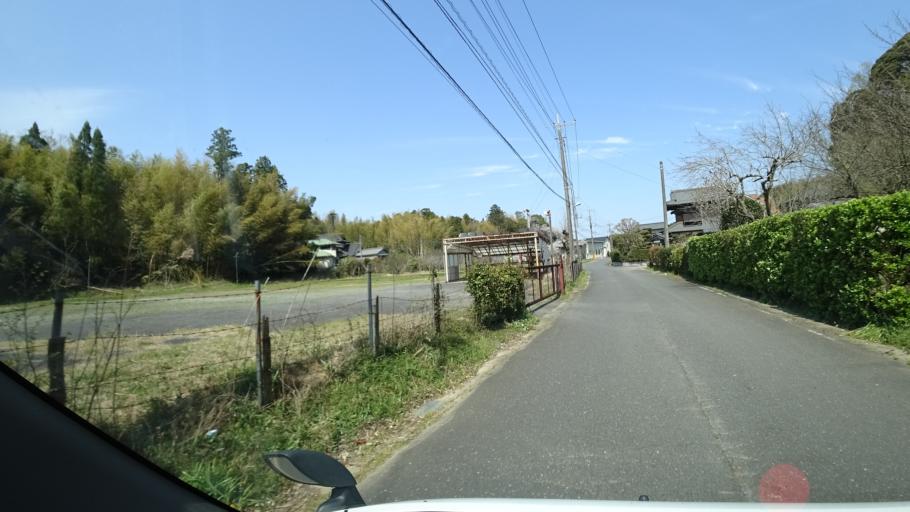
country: JP
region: Chiba
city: Narita
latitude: 35.7862
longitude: 140.3503
